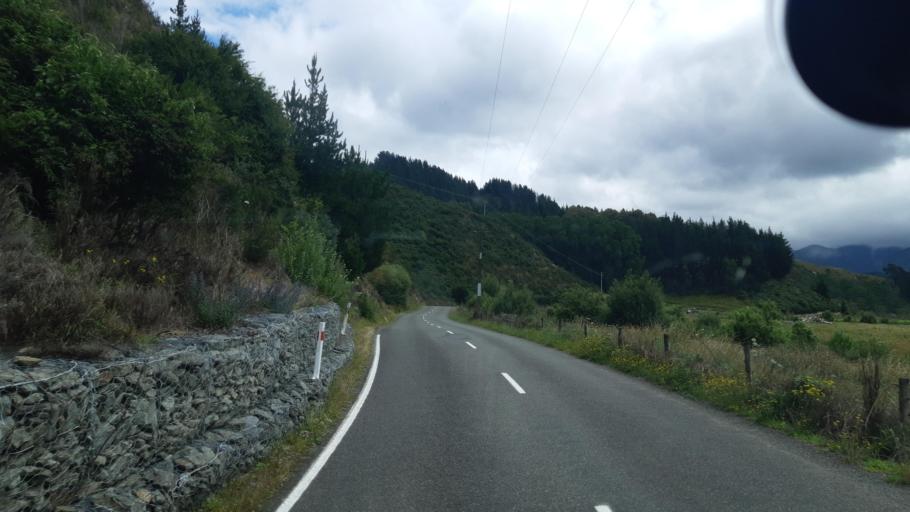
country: NZ
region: Marlborough
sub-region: Marlborough District
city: Blenheim
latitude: -41.4857
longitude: 173.7470
